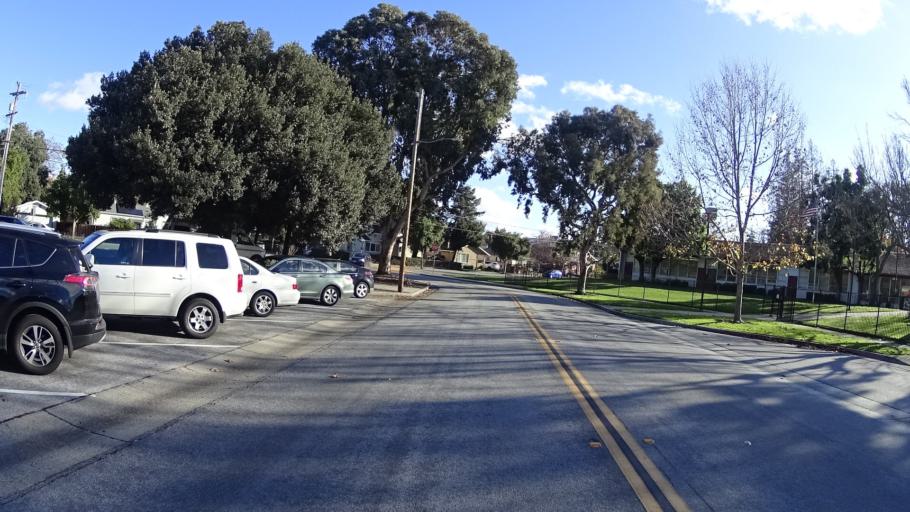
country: US
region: California
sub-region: Santa Clara County
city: Sunnyvale
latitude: 37.3763
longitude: -122.0395
